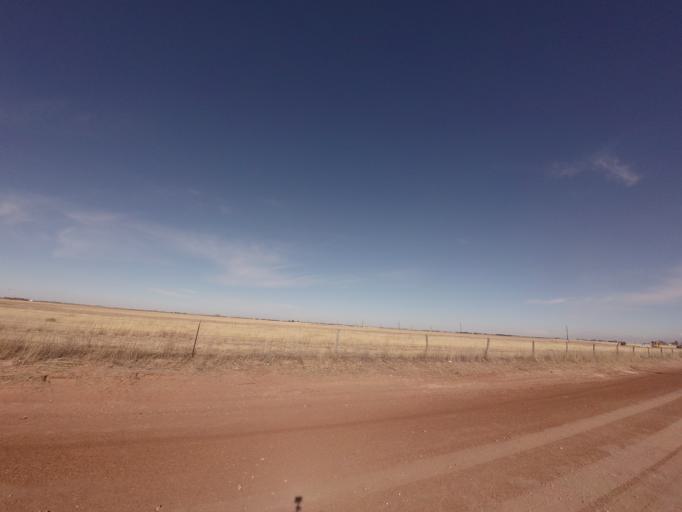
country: US
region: New Mexico
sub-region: Curry County
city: Clovis
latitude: 34.4048
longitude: -103.1279
